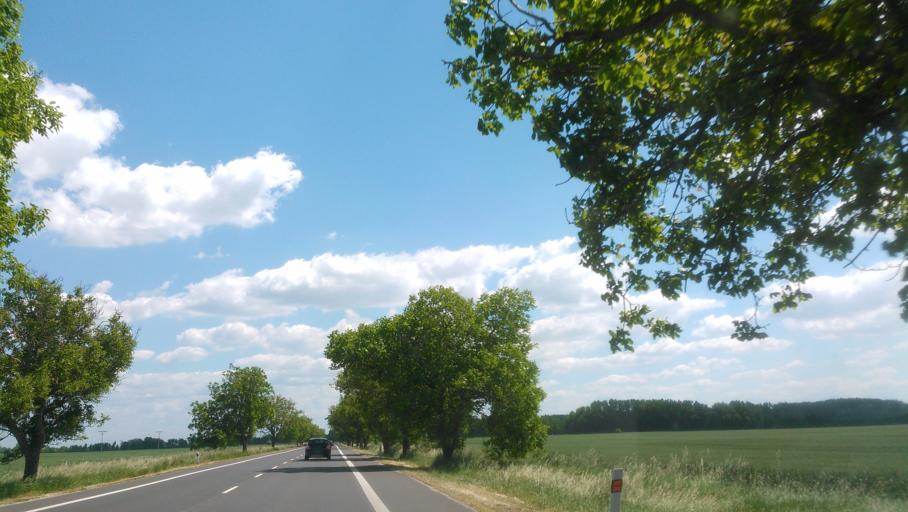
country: SK
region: Trnavsky
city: Dunajska Streda
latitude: 47.9583
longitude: 17.6983
